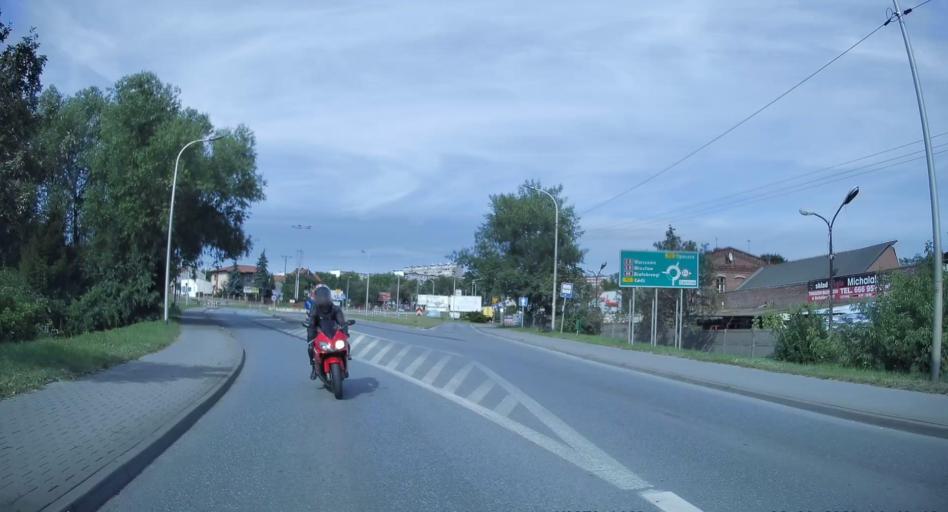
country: PL
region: Lodz Voivodeship
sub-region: Powiat tomaszowski
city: Tomaszow Mazowiecki
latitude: 51.5382
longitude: 20.0010
